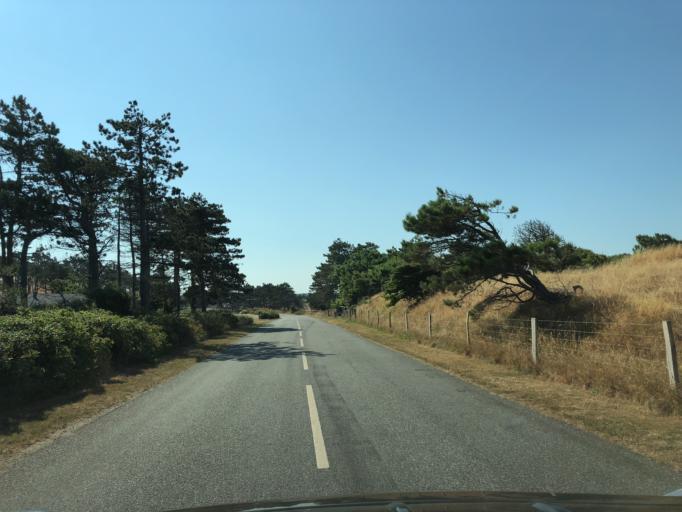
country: DK
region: Zealand
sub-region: Odsherred Kommune
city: Asnaes
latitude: 56.0070
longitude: 11.2792
